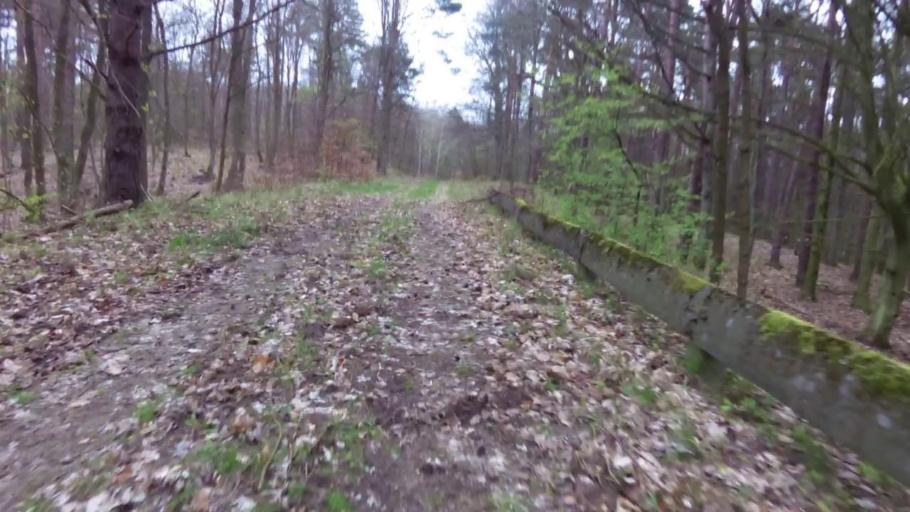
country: PL
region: West Pomeranian Voivodeship
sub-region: Powiat kamienski
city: Wolin
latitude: 53.9871
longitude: 14.6131
